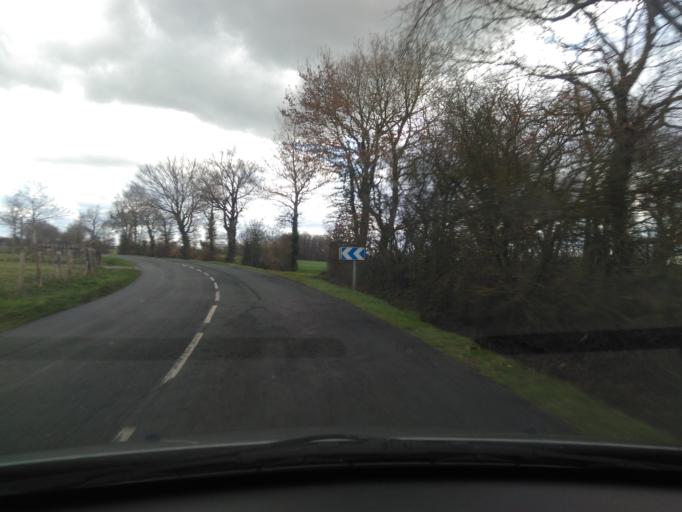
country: FR
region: Pays de la Loire
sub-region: Departement de la Vendee
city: Les Essarts
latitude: 46.7555
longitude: -1.2194
